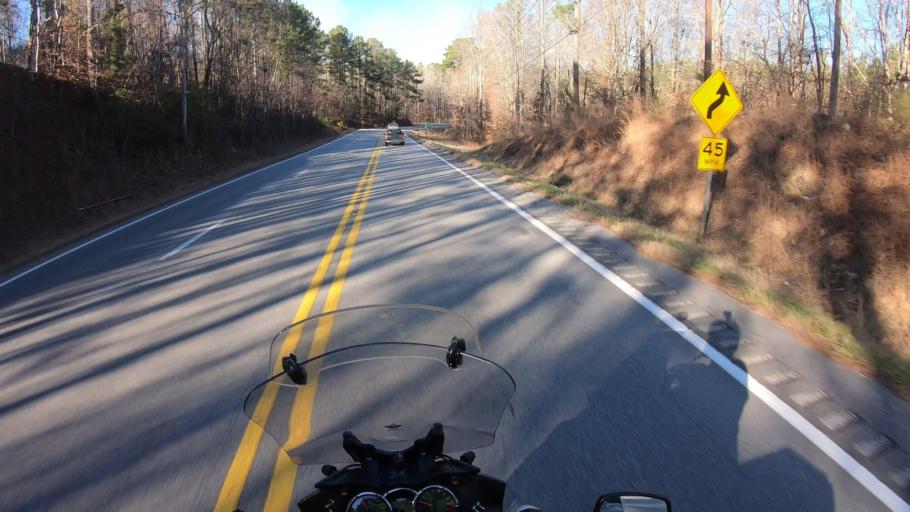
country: US
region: Alabama
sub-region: Cleburne County
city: Heflin
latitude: 33.6925
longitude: -85.5242
